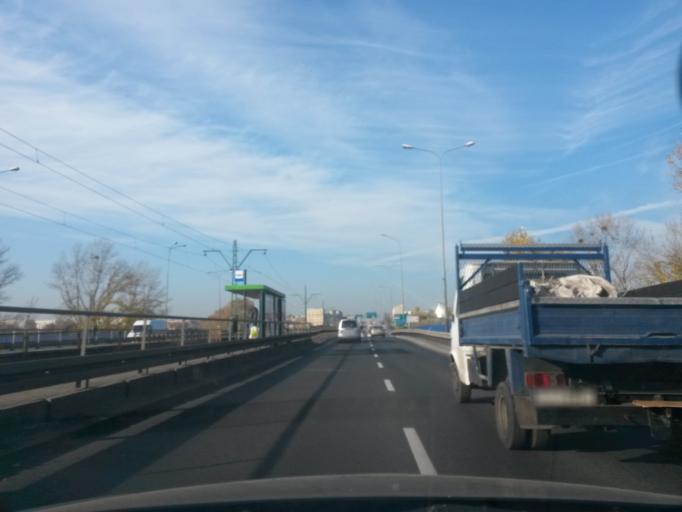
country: PL
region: Greater Poland Voivodeship
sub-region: Poznan
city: Poznan
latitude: 52.3828
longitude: 16.9296
